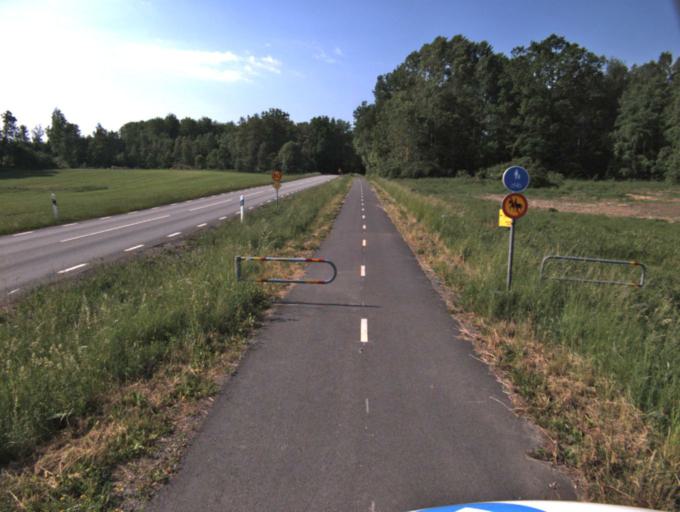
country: SE
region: Skane
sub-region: Kristianstads Kommun
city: Tollarp
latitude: 56.1503
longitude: 14.2614
